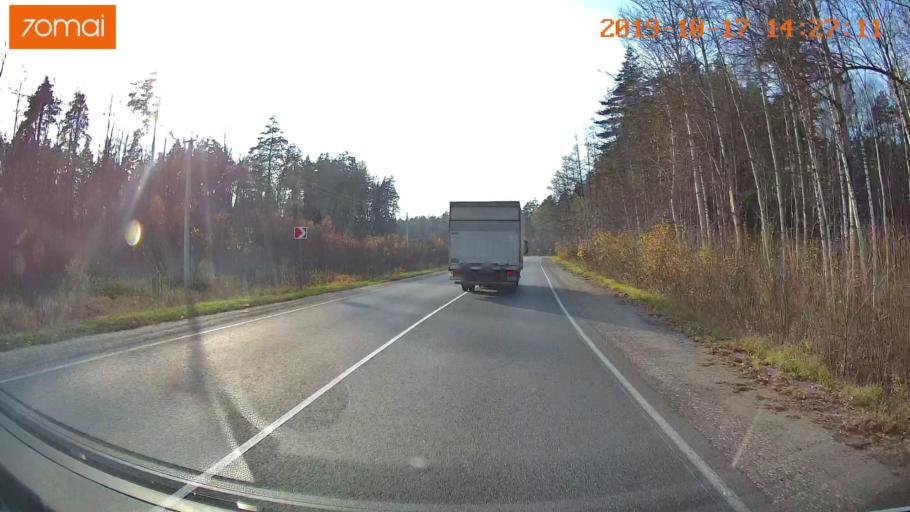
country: RU
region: Moskovskaya
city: Radovitskiy
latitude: 54.9876
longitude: 39.9567
